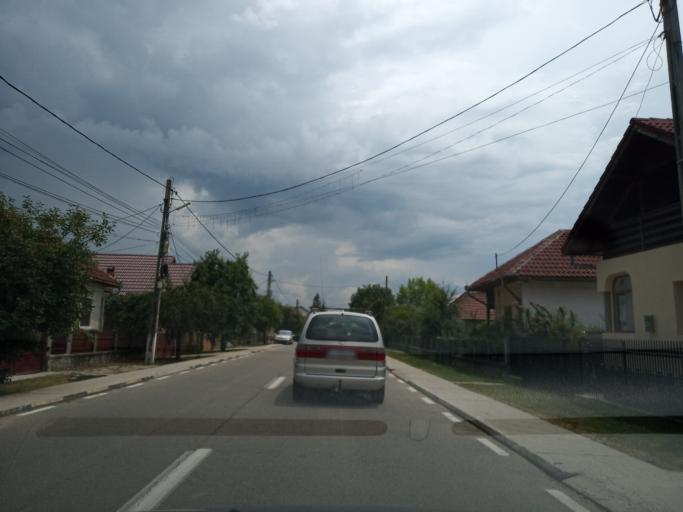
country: RO
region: Gorj
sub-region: Comuna Tismana
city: Tismana
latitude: 45.0525
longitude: 22.9461
